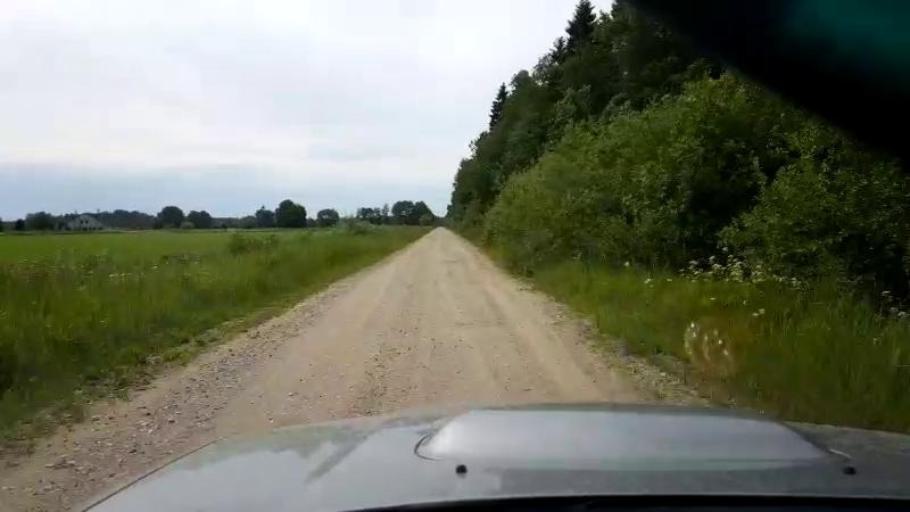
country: EE
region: Paernumaa
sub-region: Tootsi vald
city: Tootsi
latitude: 58.5268
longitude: 24.7183
